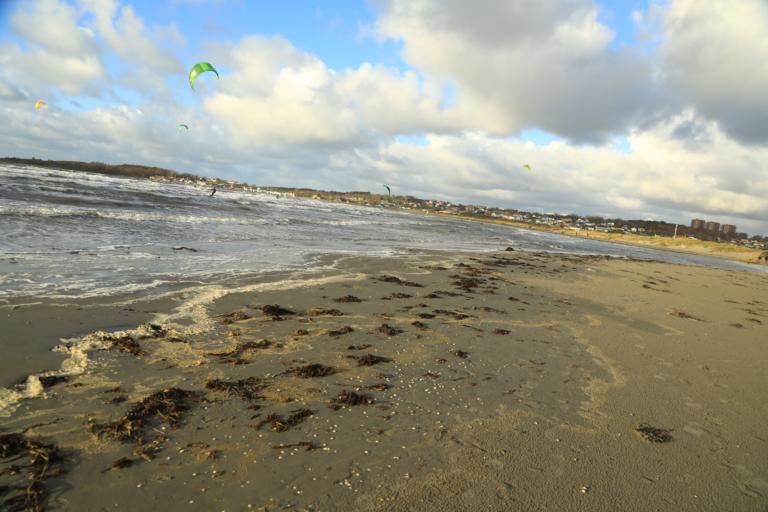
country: SE
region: Halland
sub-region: Varbergs Kommun
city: Traslovslage
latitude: 57.0781
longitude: 12.2612
